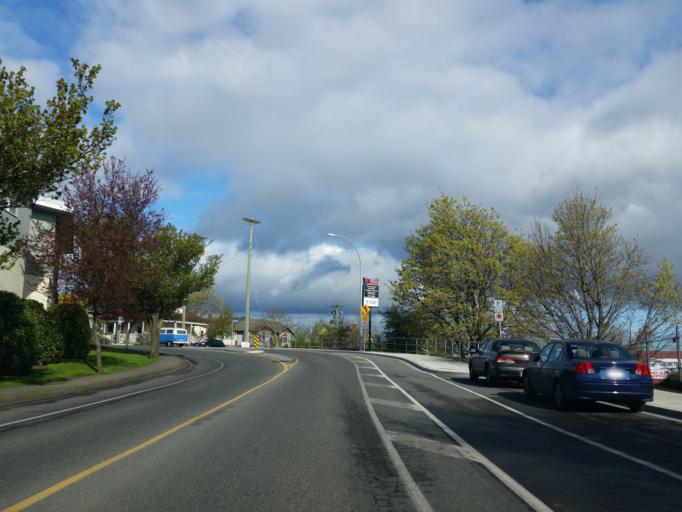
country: CA
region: British Columbia
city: Victoria
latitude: 48.4350
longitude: -123.3825
